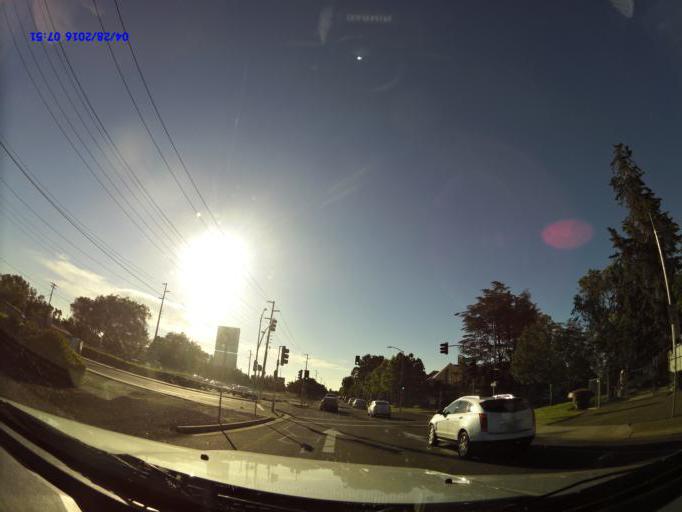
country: US
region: California
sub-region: Stanislaus County
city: Modesto
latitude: 37.6683
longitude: -120.9853
